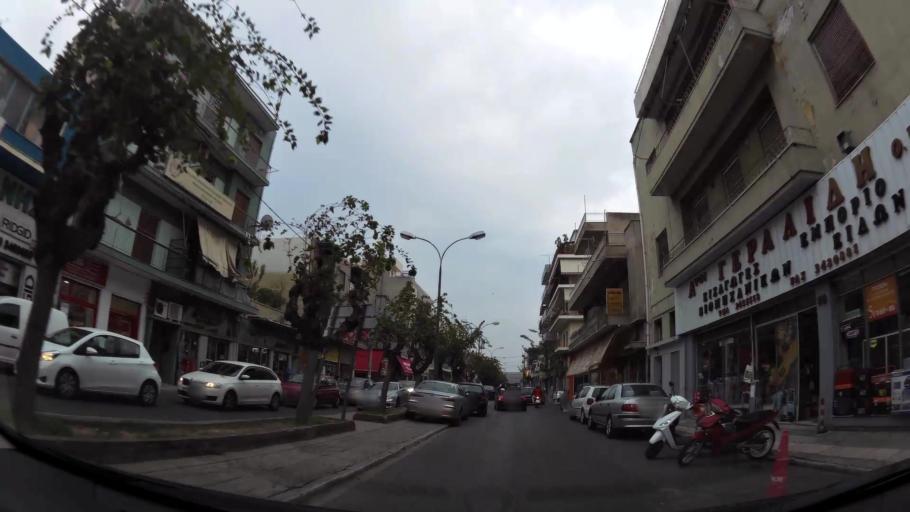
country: GR
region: Attica
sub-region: Nomarchia Athinas
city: Athens
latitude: 37.9845
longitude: 23.7102
